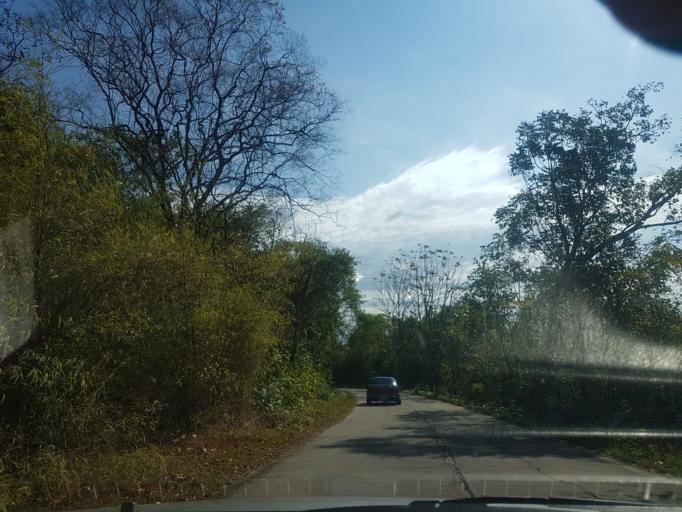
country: TH
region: Lop Buri
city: Lop Buri
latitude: 14.8228
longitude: 100.7524
